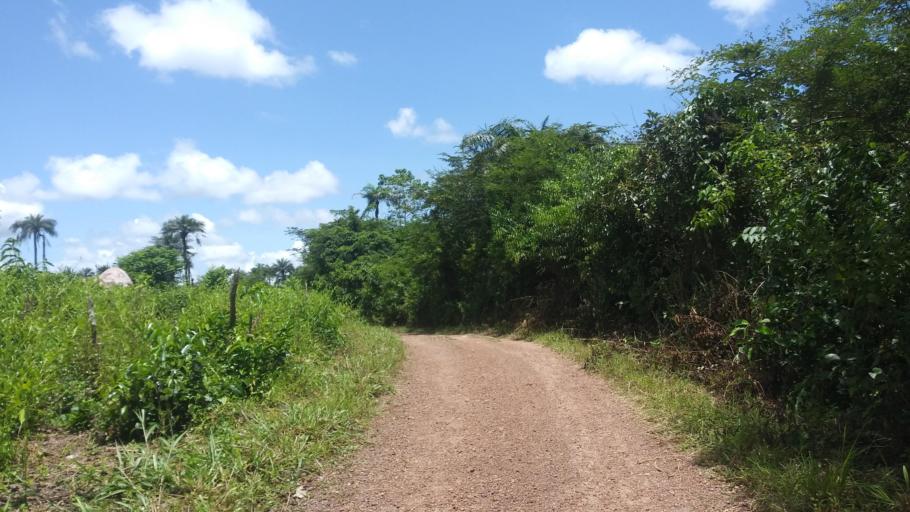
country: SL
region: Northern Province
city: Makeni
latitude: 8.8944
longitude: -12.0026
